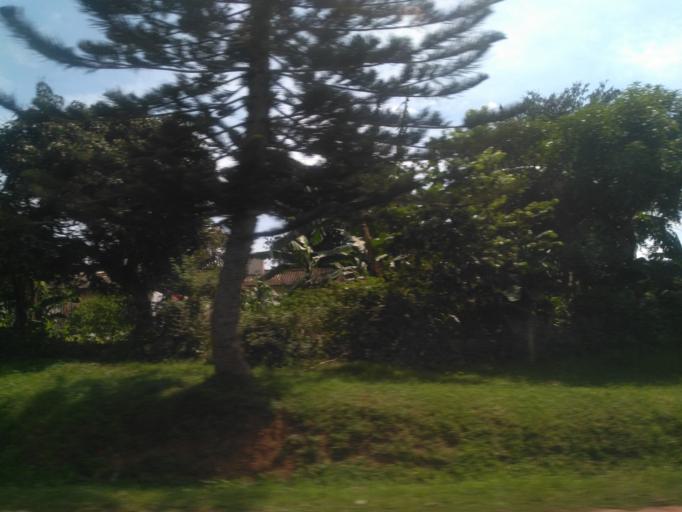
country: UG
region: Central Region
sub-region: Wakiso District
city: Entebbe
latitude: 0.0494
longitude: 32.4567
